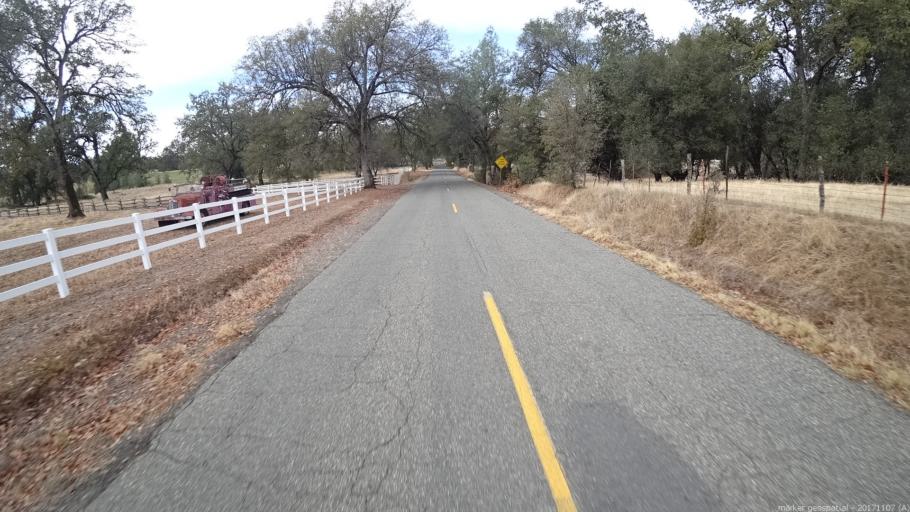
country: US
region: California
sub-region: Shasta County
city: Shasta
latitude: 40.5012
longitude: -122.5655
